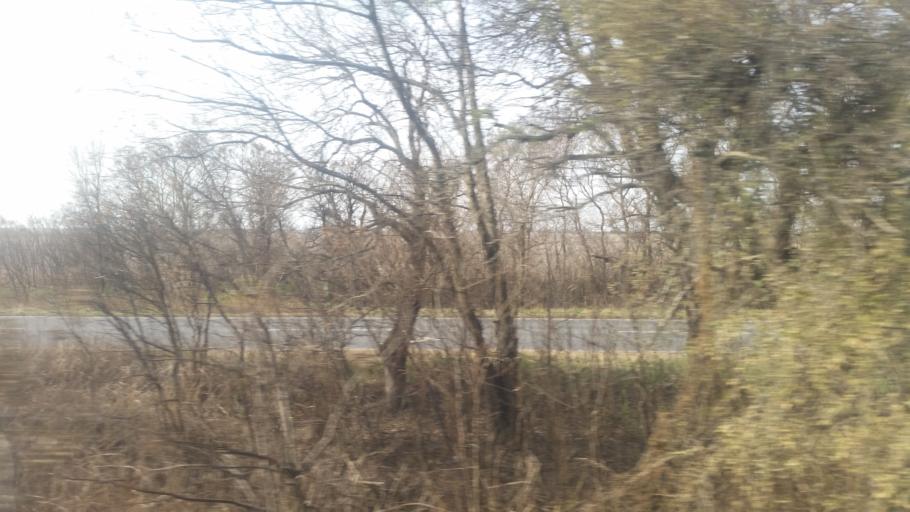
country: AR
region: Cordoba
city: Laguna Larga
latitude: -31.7314
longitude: -63.8429
